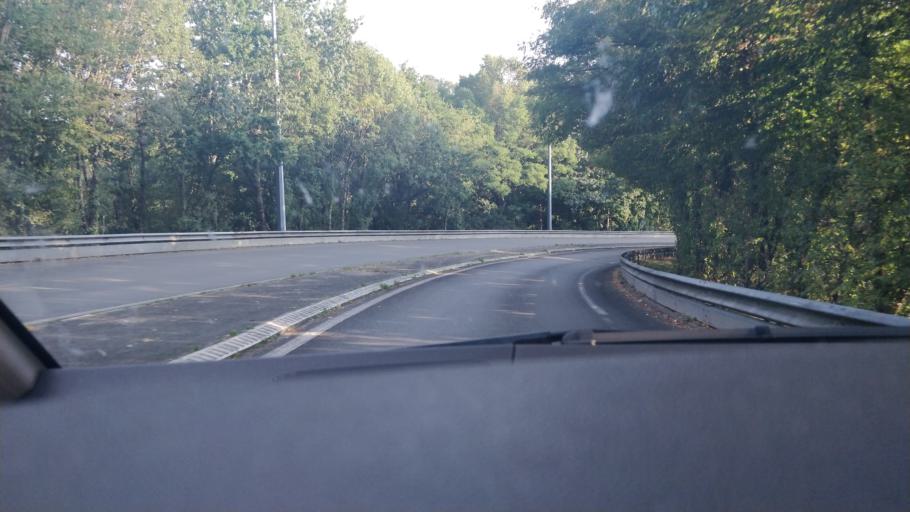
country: FR
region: Limousin
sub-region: Departement de la Haute-Vienne
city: Limoges
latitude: 45.8412
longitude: 1.2878
